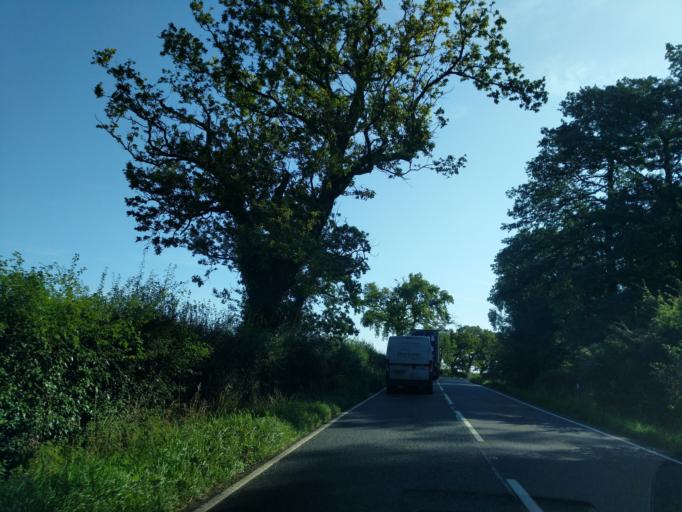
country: GB
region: England
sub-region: Lincolnshire
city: Bourne
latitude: 52.8011
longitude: -0.4639
